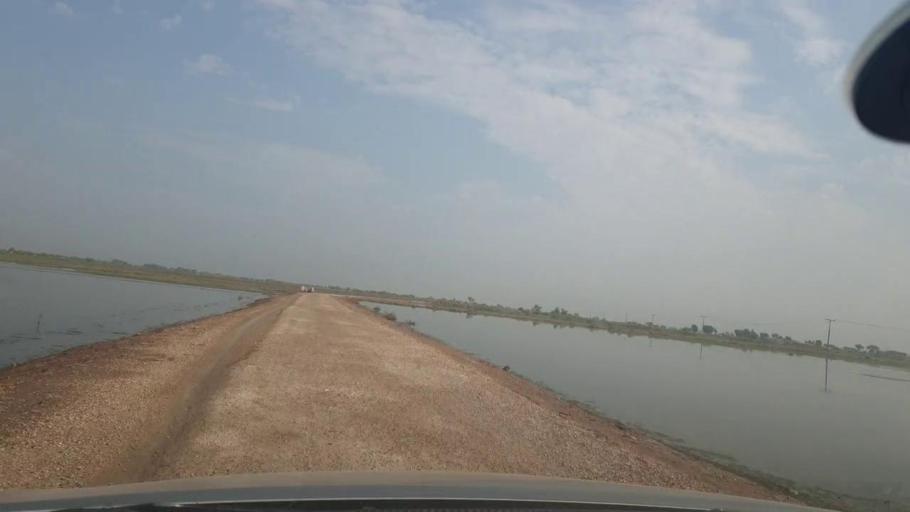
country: PK
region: Balochistan
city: Mehrabpur
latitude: 28.0620
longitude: 68.2104
